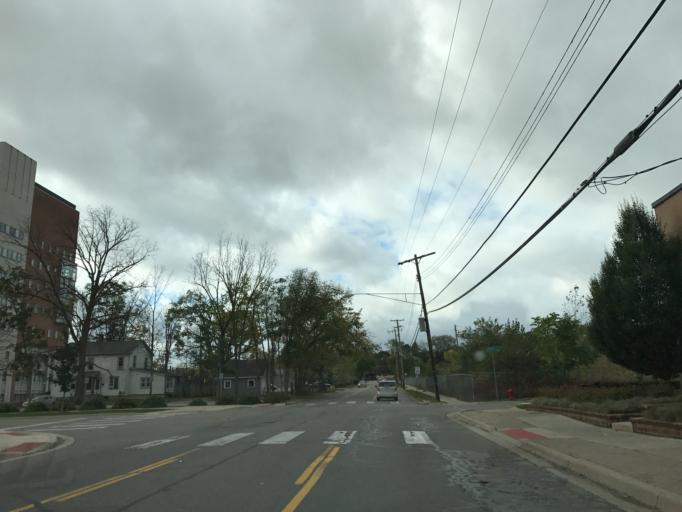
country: US
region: Michigan
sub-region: Washtenaw County
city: Ann Arbor
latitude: 42.2885
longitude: -83.7353
